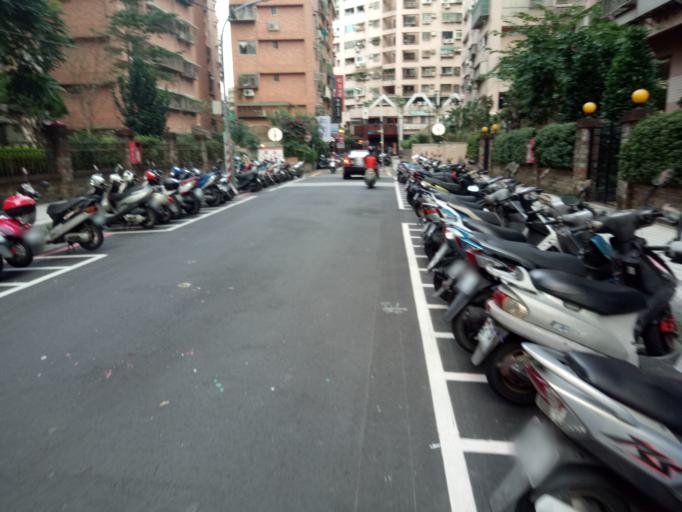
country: TW
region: Taipei
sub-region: Taipei
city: Banqiao
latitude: 25.0502
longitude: 121.4457
